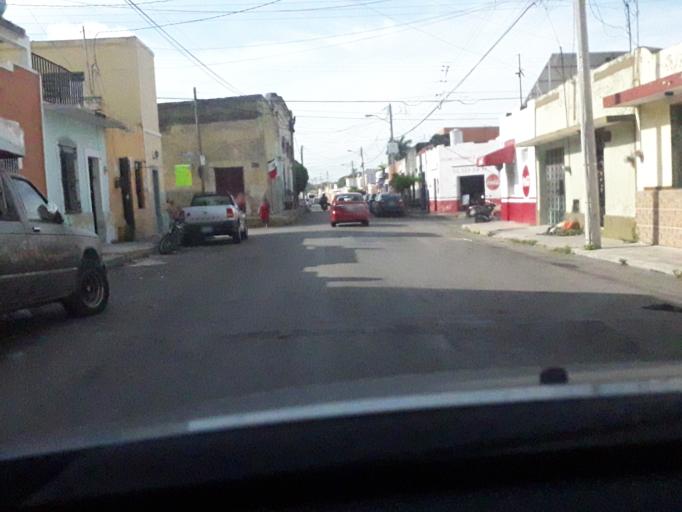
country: MX
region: Yucatan
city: Merida
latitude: 20.9568
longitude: -89.6140
